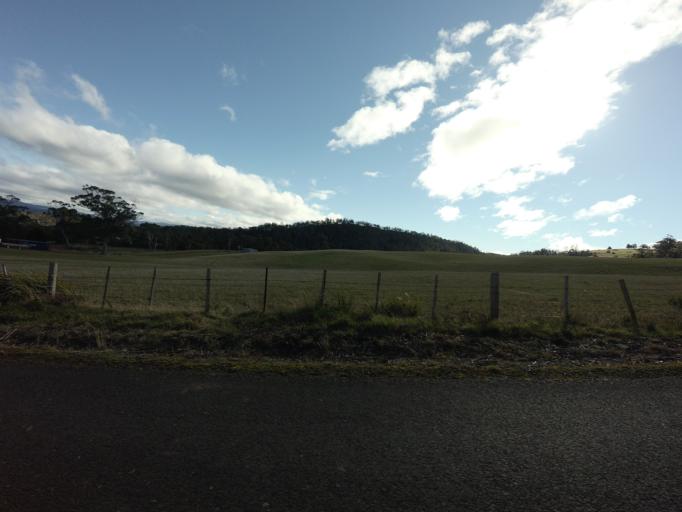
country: AU
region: Tasmania
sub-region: Derwent Valley
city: New Norfolk
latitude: -42.7244
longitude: 147.0322
